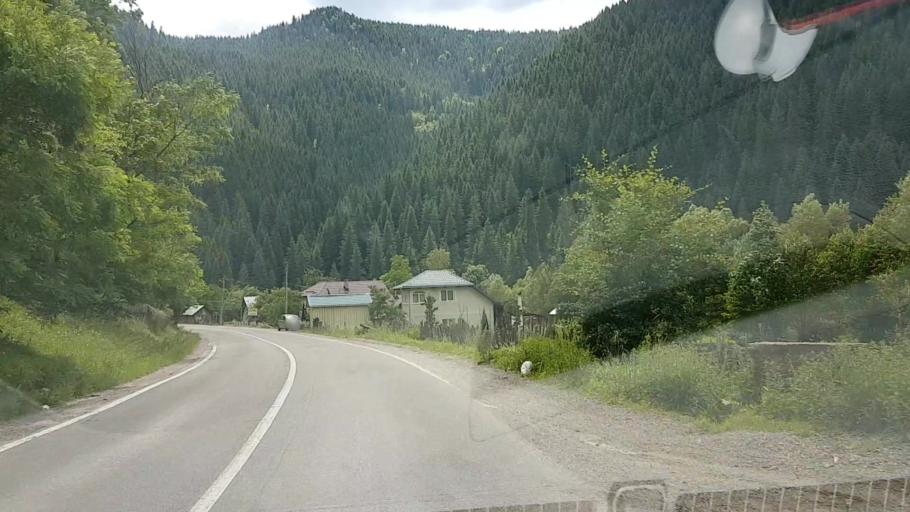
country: RO
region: Suceava
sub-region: Comuna Brosteni
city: Brosteni
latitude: 47.2194
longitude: 25.7378
